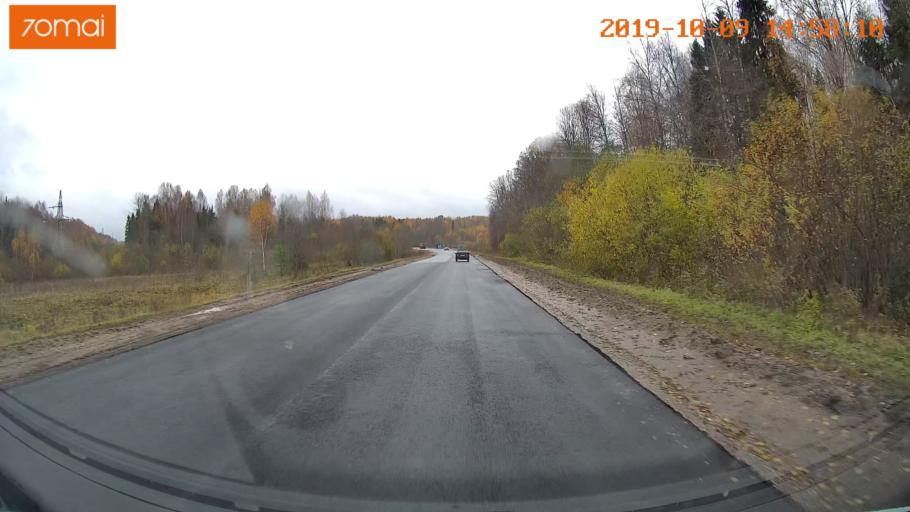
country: RU
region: Kostroma
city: Chistyye Bory
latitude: 58.3295
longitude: 41.6538
